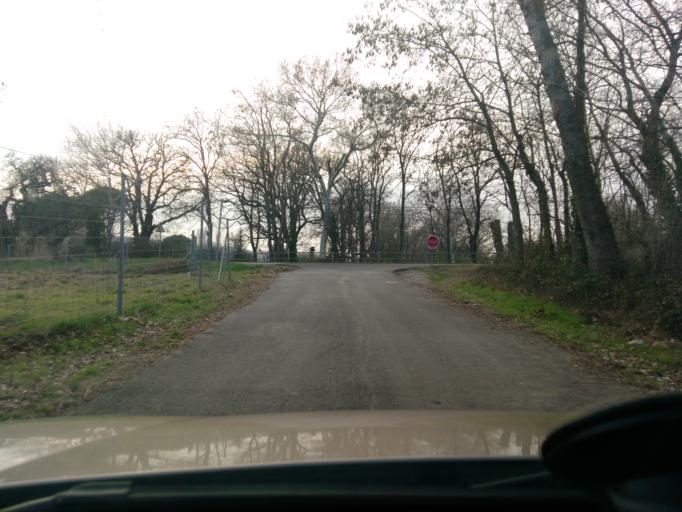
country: FR
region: Rhone-Alpes
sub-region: Departement de la Drome
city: Montboucher-sur-Jabron
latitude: 44.5453
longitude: 4.8073
